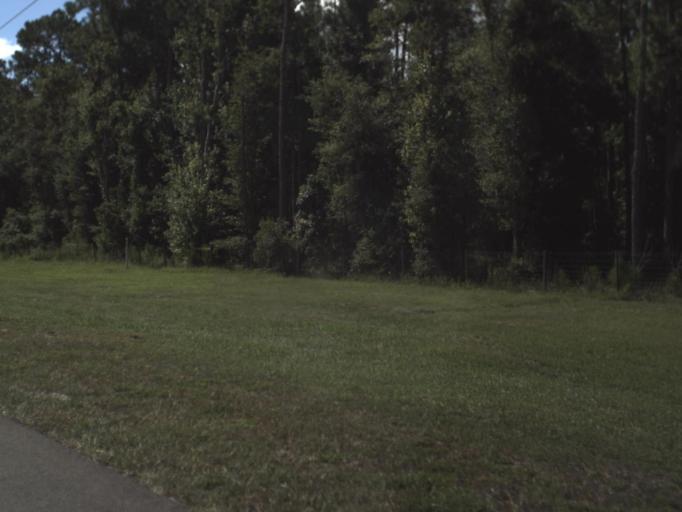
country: US
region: Florida
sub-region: Polk County
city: Kathleen
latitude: 28.2348
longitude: -82.0399
